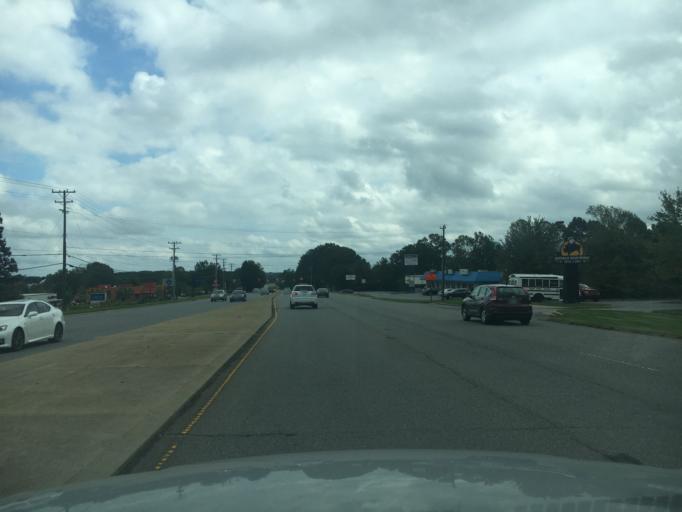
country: US
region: North Carolina
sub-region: Catawba County
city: Hickory
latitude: 35.7017
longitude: -81.2921
